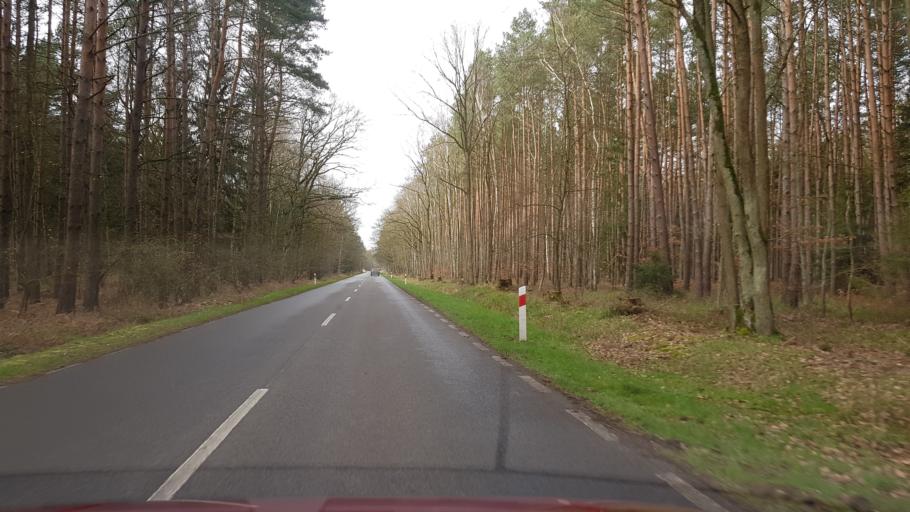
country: PL
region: West Pomeranian Voivodeship
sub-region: Powiat policki
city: Nowe Warpno
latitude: 53.6990
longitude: 14.3391
